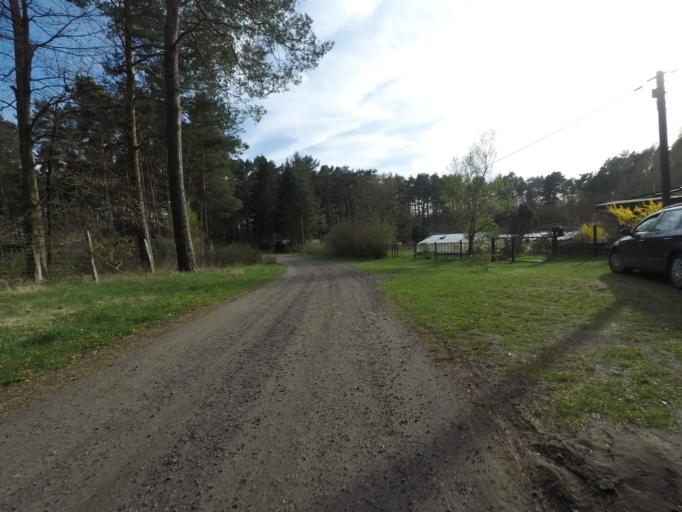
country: DE
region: Brandenburg
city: Marienwerder
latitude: 52.8479
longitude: 13.6510
